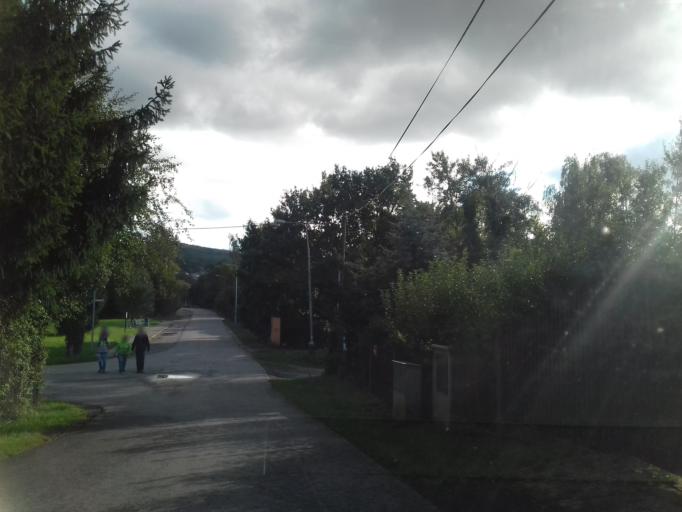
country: CZ
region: Central Bohemia
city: Revnice
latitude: 49.9186
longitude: 14.2313
